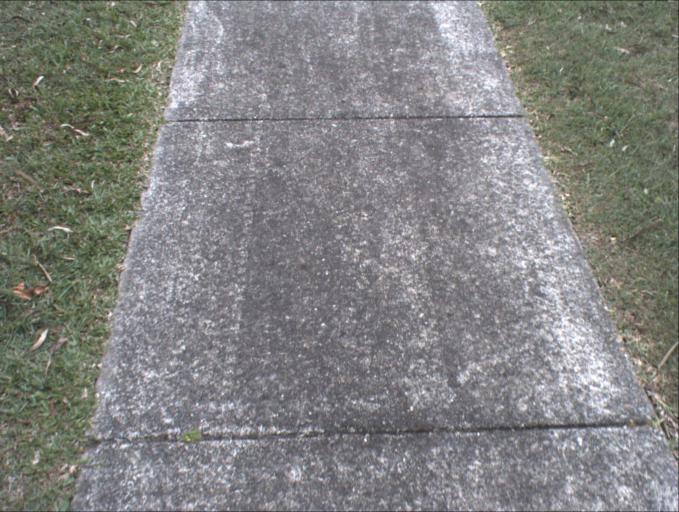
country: AU
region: Queensland
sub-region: Logan
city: Slacks Creek
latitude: -27.6559
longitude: 153.2033
